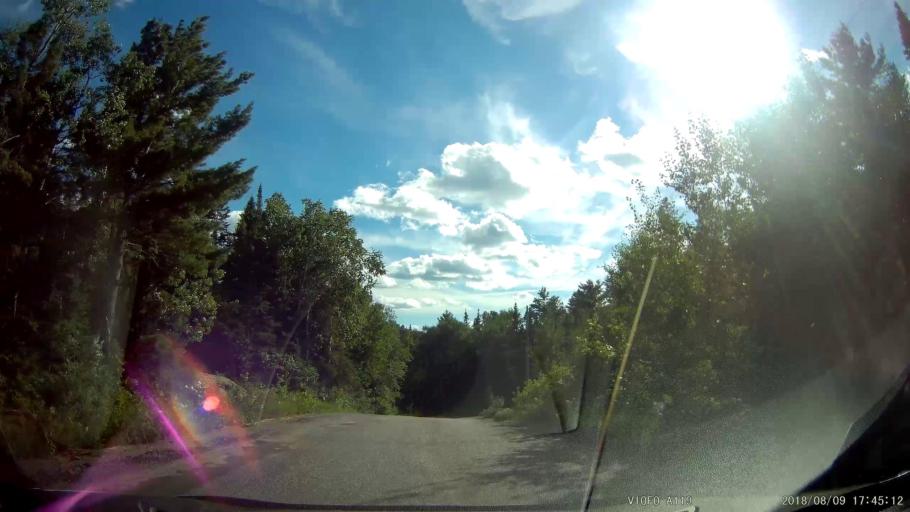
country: CA
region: Ontario
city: Rayside-Balfour
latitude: 46.6018
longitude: -81.5331
